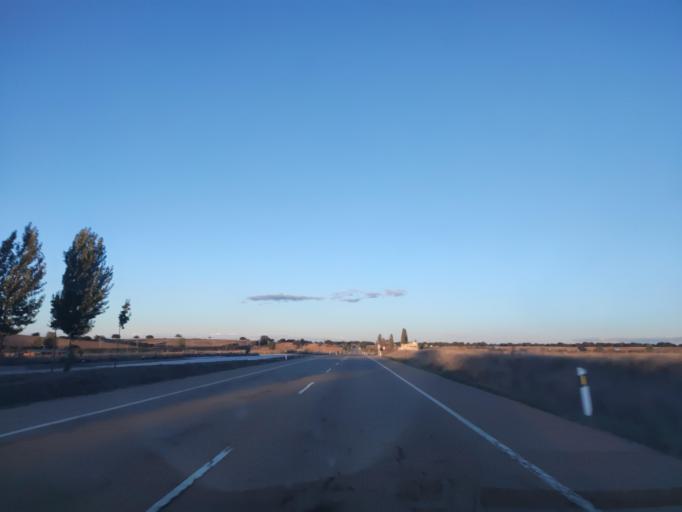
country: ES
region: Castille and Leon
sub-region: Provincia de Salamanca
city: Martin de Yeltes
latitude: 40.7763
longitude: -6.2839
